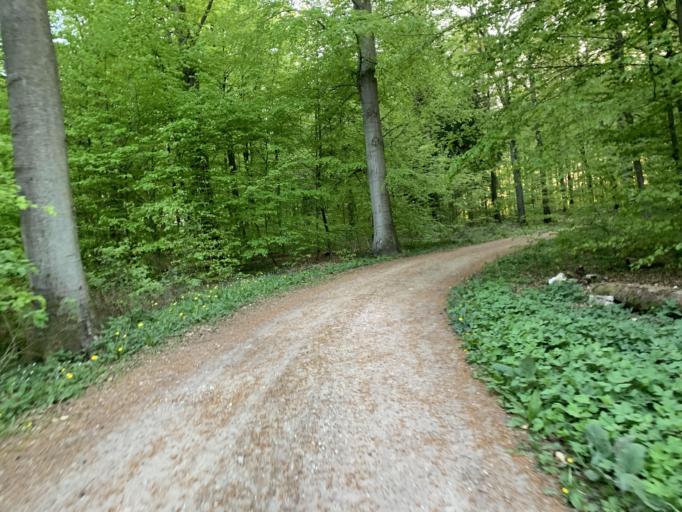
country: DE
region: Schleswig-Holstein
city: Worth
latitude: 53.4663
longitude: 10.4264
